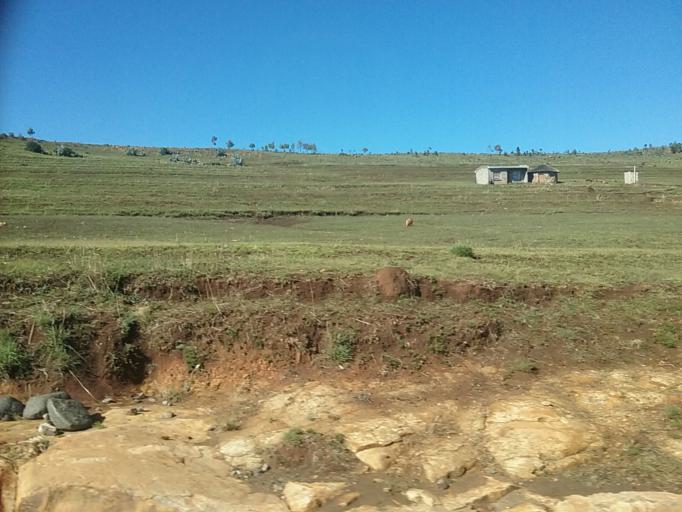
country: LS
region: Berea
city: Teyateyaneng
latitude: -29.2315
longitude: 27.8883
